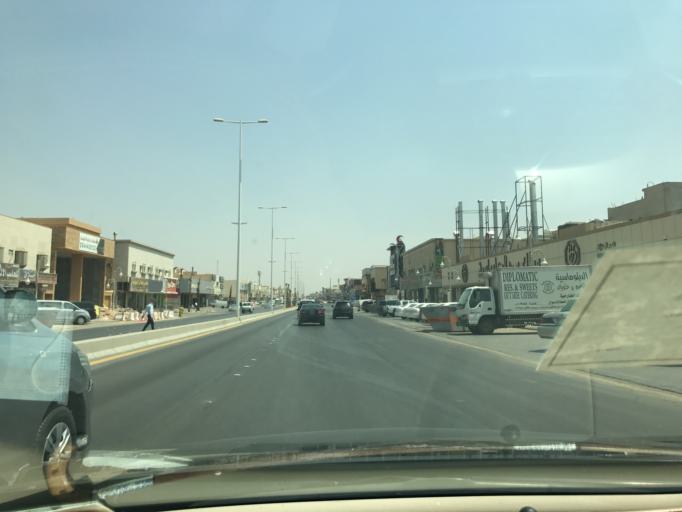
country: SA
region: Ar Riyad
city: Riyadh
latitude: 24.7487
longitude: 46.7629
